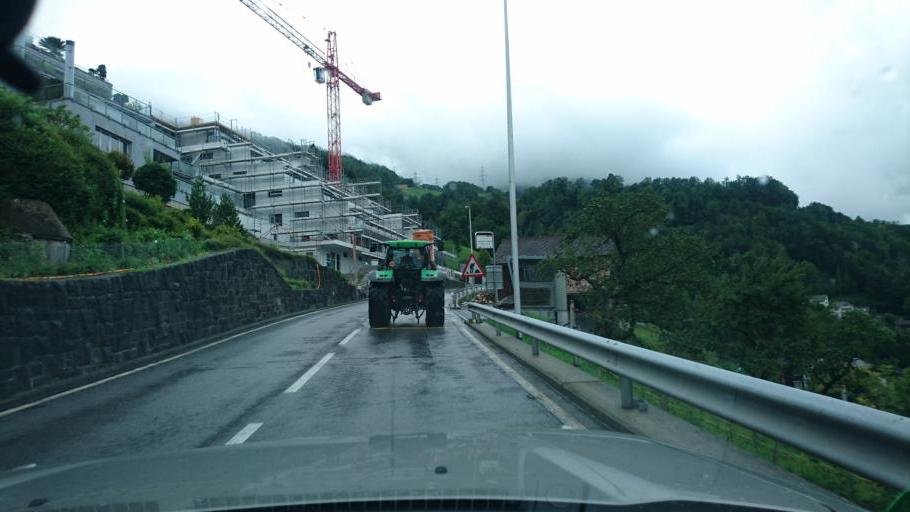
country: CH
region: Saint Gallen
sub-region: Wahlkreis See-Gaster
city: Amden
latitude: 47.1157
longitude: 9.1769
